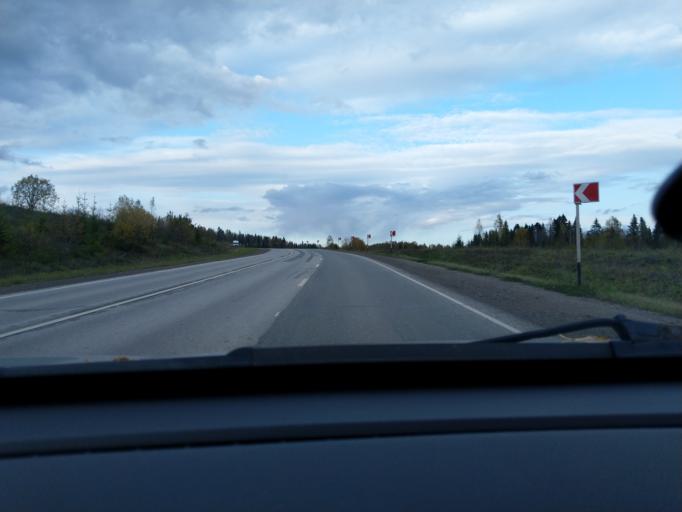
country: RU
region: Perm
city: Dobryanka
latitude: 58.4316
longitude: 56.5386
